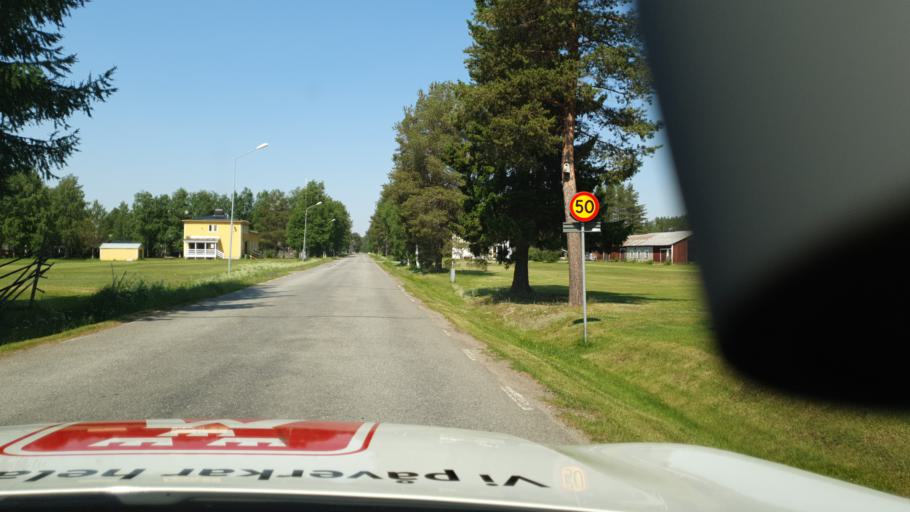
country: SE
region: Vaesterbotten
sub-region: Skelleftea Kommun
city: Langsele
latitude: 64.9507
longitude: 19.9265
